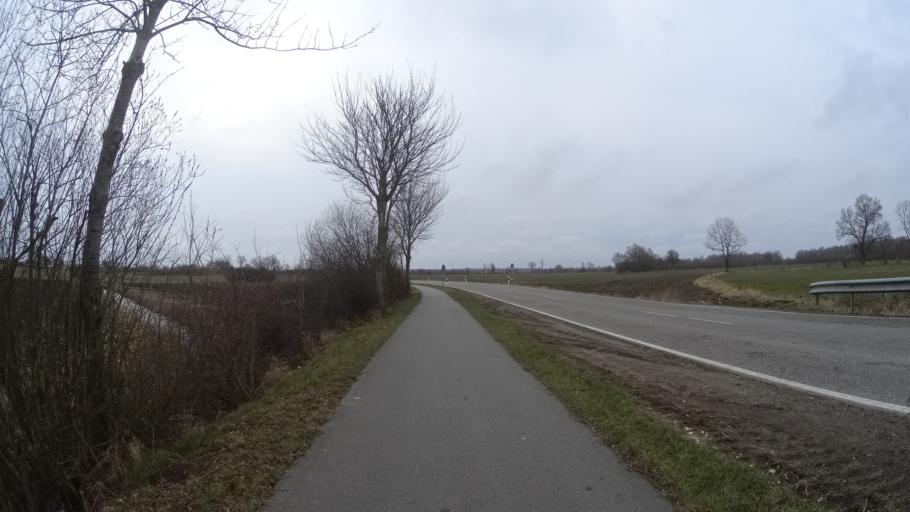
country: DE
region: Schleswig-Holstein
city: Krummbek
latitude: 54.4099
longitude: 10.4156
